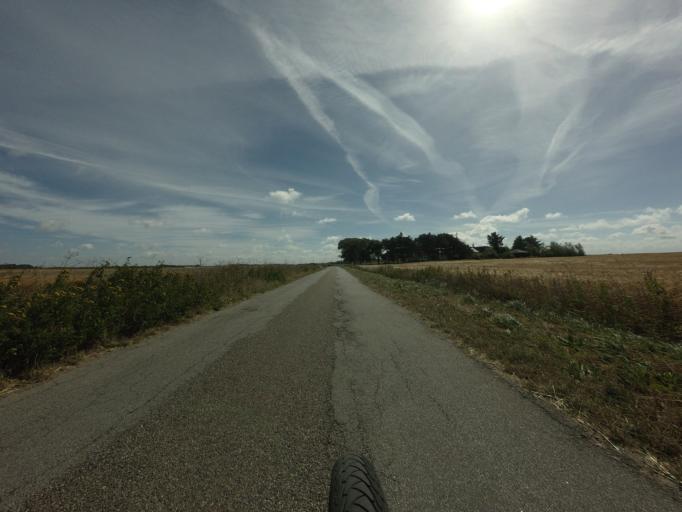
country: DK
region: North Denmark
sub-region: Hjorring Kommune
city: Vra
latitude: 57.3423
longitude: 9.7959
